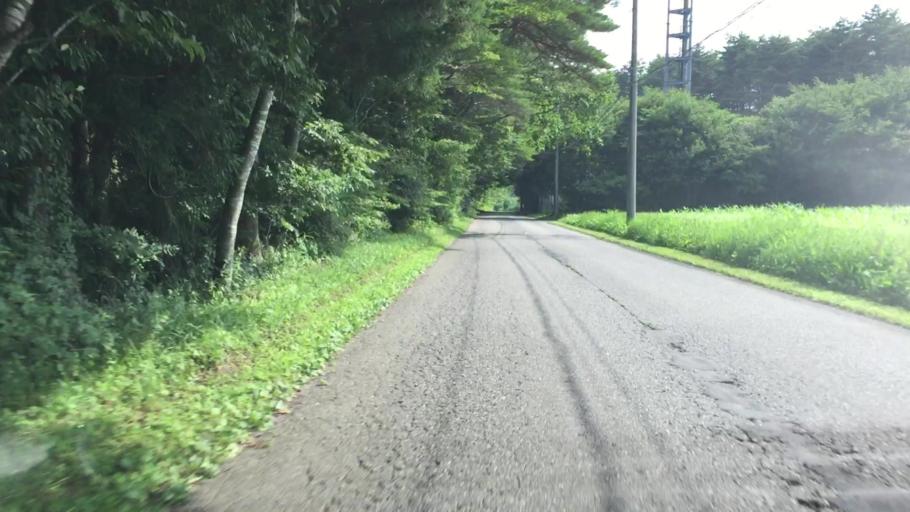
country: JP
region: Tochigi
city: Kuroiso
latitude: 37.0404
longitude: 139.9520
